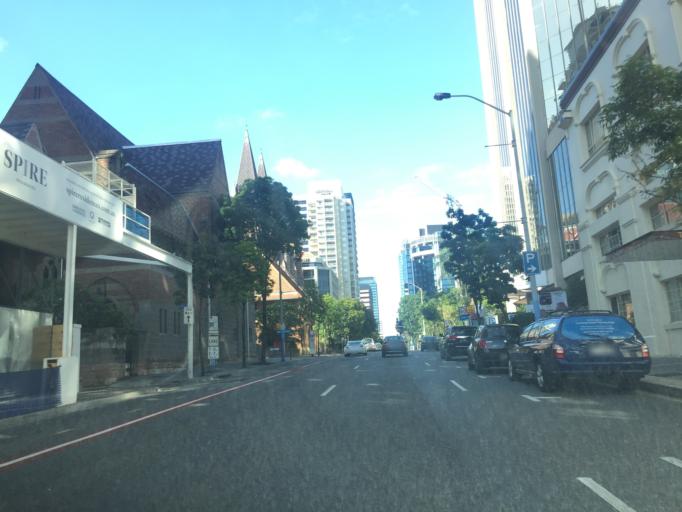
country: AU
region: Queensland
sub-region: Brisbane
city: Fortitude Valley
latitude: -27.4627
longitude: 153.0307
